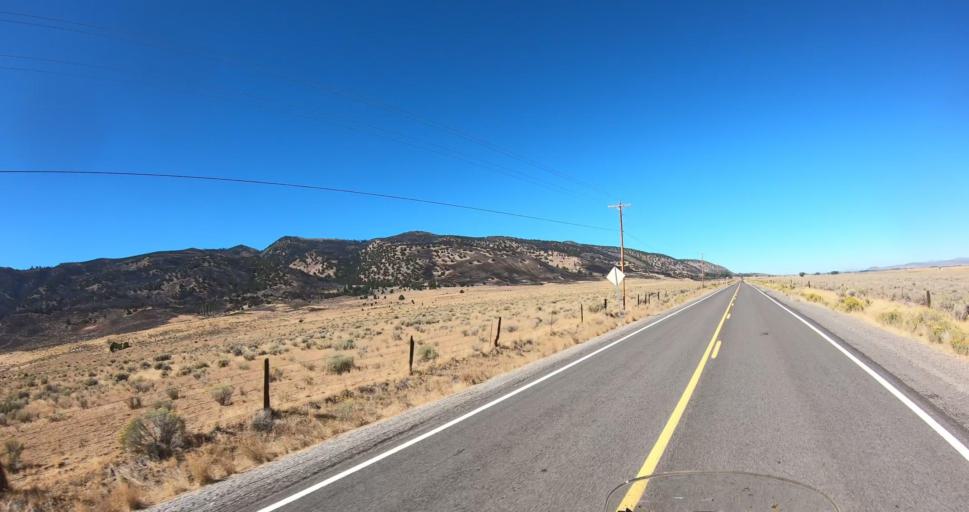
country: US
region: Oregon
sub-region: Lake County
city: Lakeview
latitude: 42.6214
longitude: -120.5058
